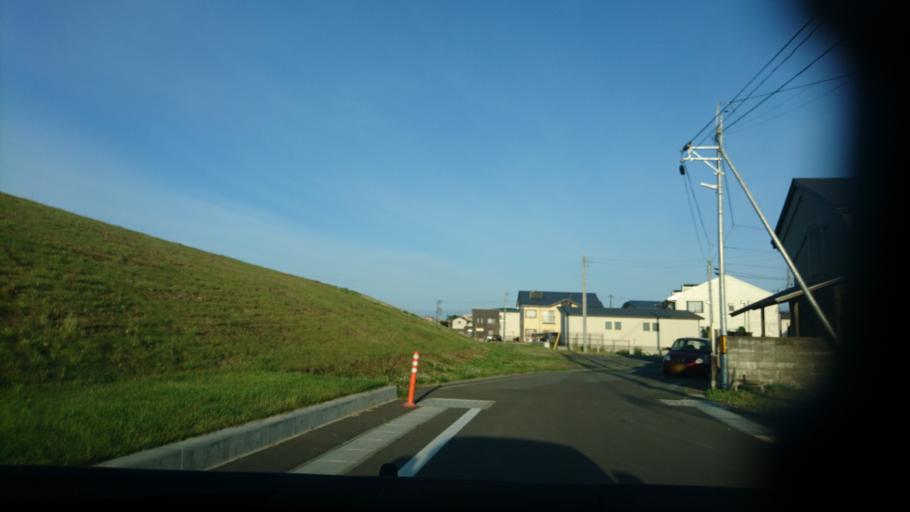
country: JP
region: Iwate
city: Ichinoseki
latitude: 38.9368
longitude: 141.1336
